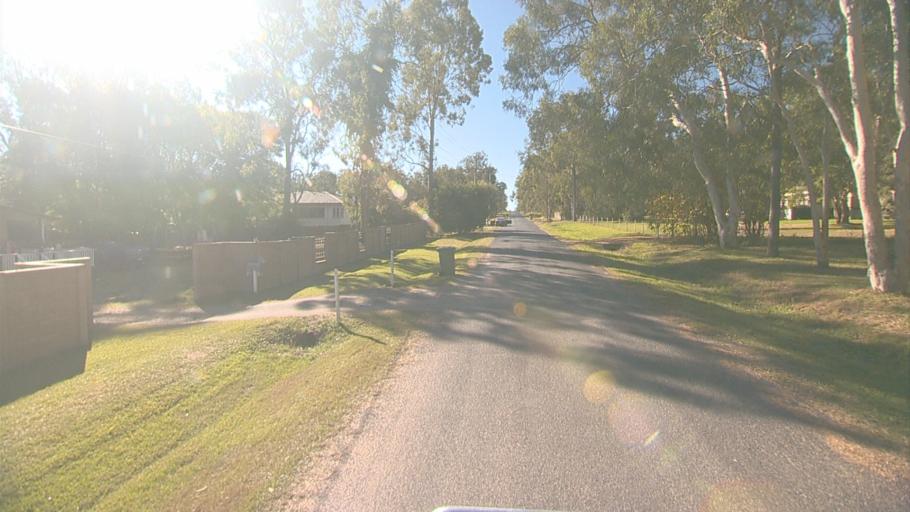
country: AU
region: Queensland
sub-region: Logan
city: Park Ridge South
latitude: -27.7312
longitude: 153.0113
